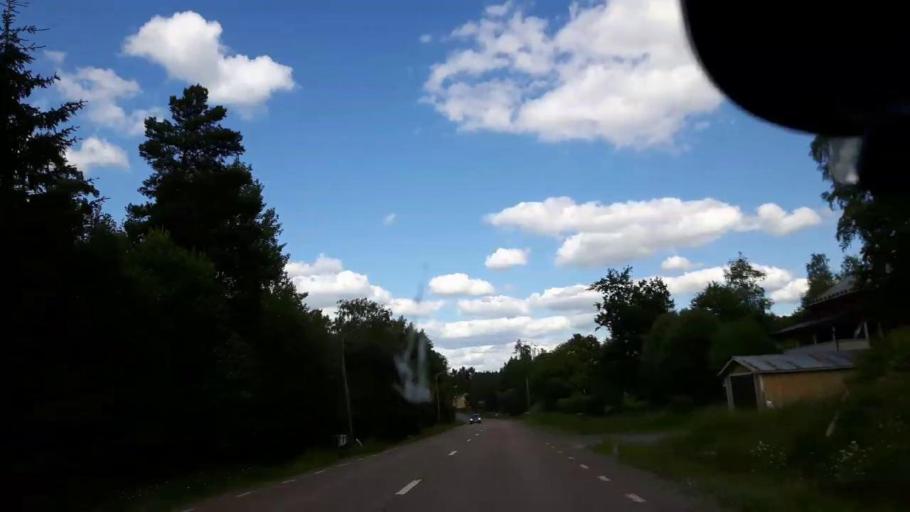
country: SE
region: Jaemtland
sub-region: Ragunda Kommun
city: Hammarstrand
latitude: 62.9959
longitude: 16.6770
